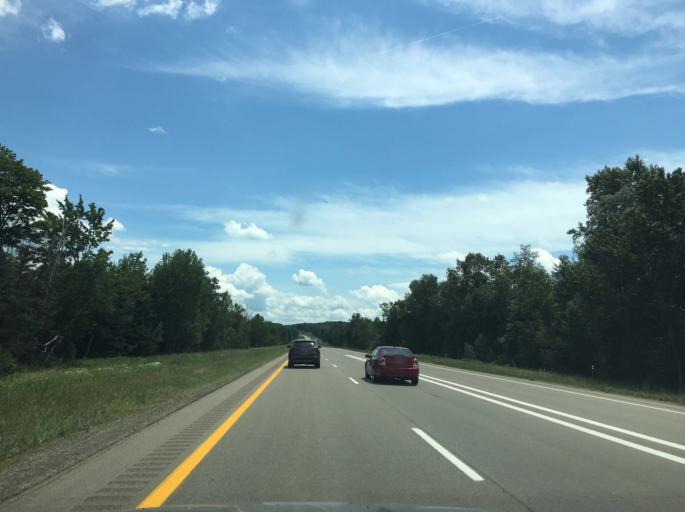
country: US
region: Michigan
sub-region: Roscommon County
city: Roscommon
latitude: 44.5067
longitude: -84.6582
